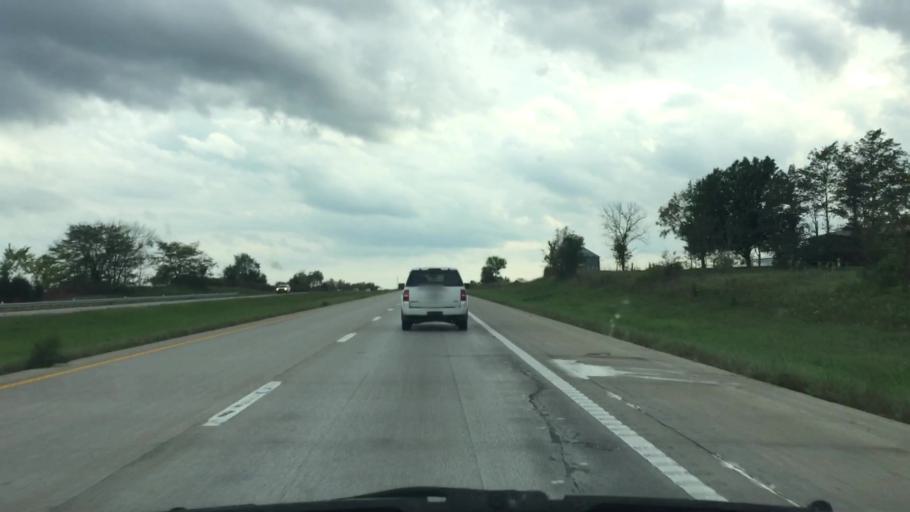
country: US
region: Missouri
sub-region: Clinton County
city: Cameron
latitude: 39.6500
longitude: -94.2404
